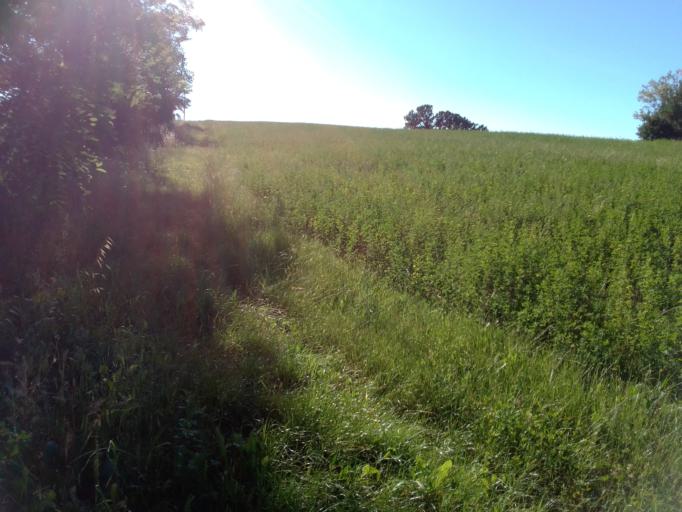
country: IT
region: Emilia-Romagna
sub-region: Provincia di Piacenza
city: Borgonovo Valtidone
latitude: 45.0065
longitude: 9.4230
